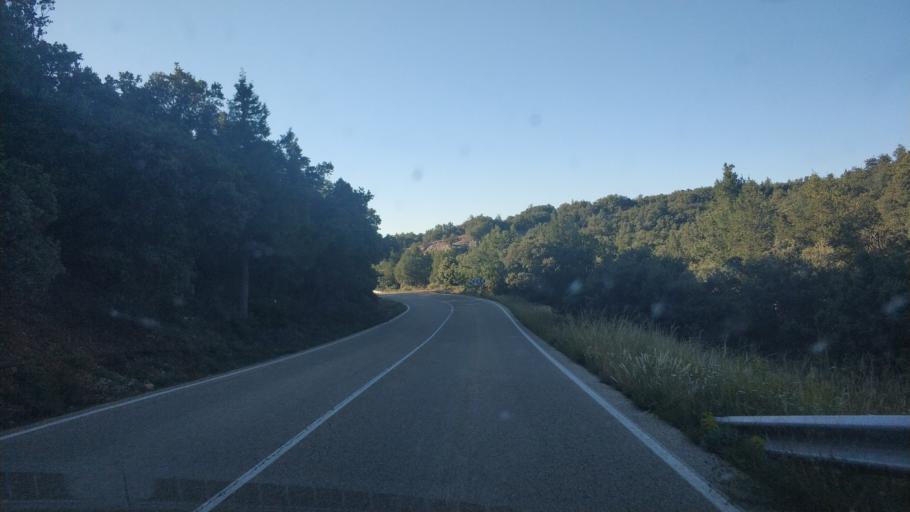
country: ES
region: Castille and Leon
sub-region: Provincia de Soria
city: Montejo de Tiermes
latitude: 41.4180
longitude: -3.2044
